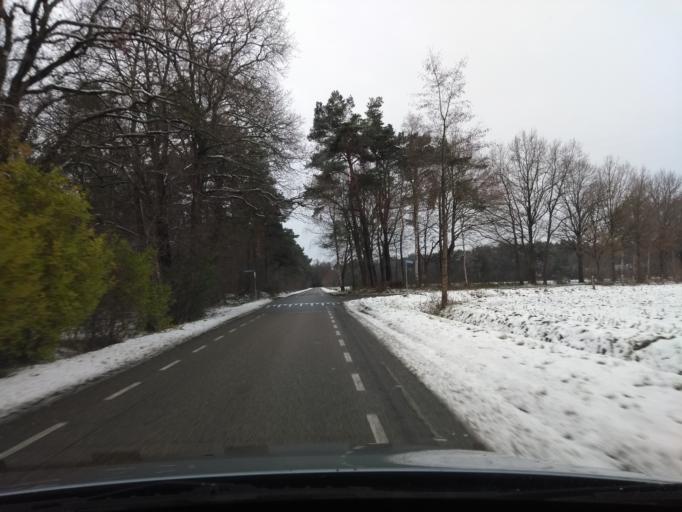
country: NL
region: Overijssel
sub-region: Gemeente Haaksbergen
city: Haaksbergen
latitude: 52.1361
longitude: 6.7459
